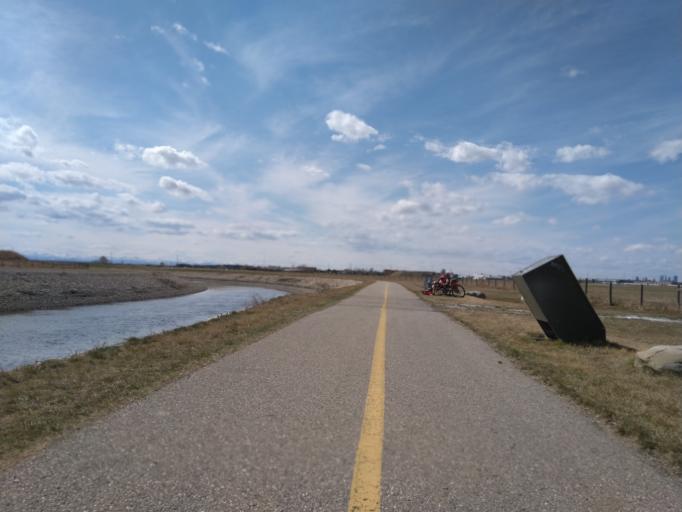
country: CA
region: Alberta
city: Chestermere
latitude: 50.9739
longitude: -113.9234
